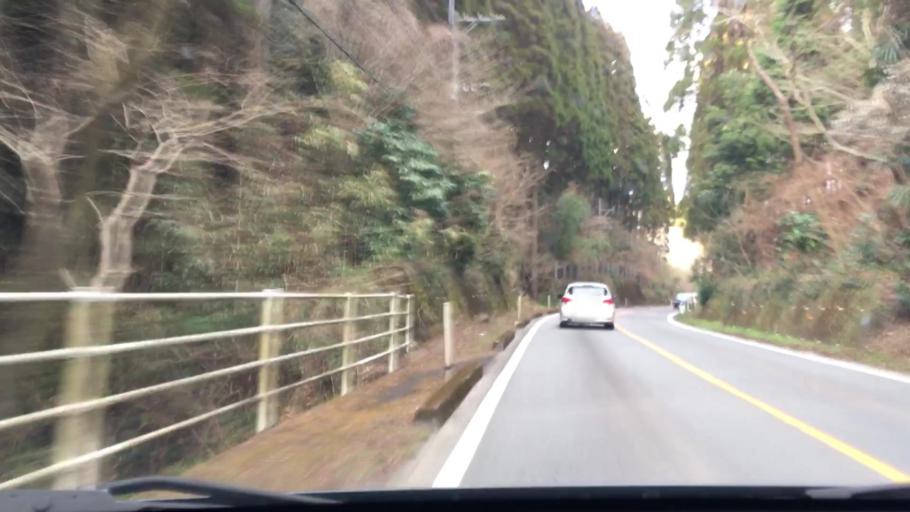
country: JP
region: Miyazaki
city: Nichinan
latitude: 31.7275
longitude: 131.3303
